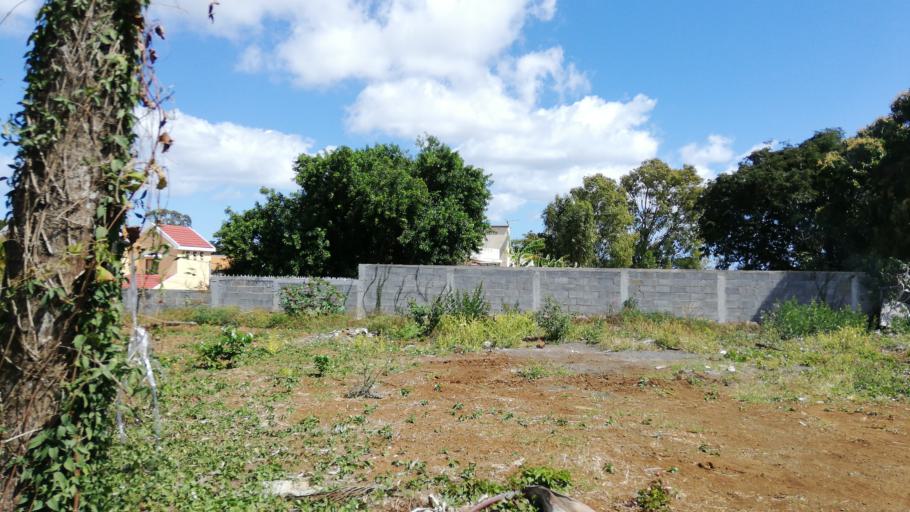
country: MU
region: Moka
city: Moka
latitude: -20.2243
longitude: 57.4719
